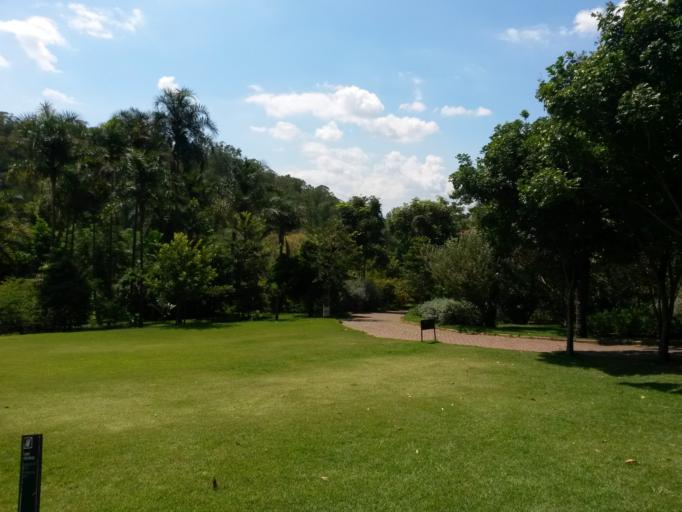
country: BR
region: Minas Gerais
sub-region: Brumadinho
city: Brumadinho
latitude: -20.1216
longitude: -44.2245
